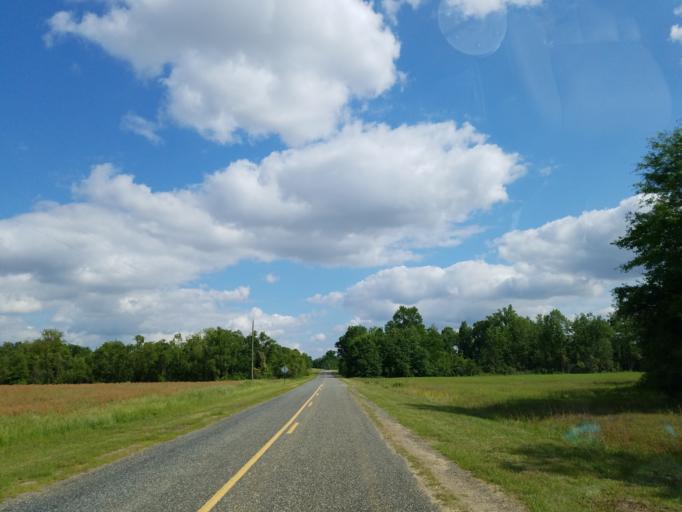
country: US
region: Georgia
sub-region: Dooly County
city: Unadilla
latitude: 32.2504
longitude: -83.7830
